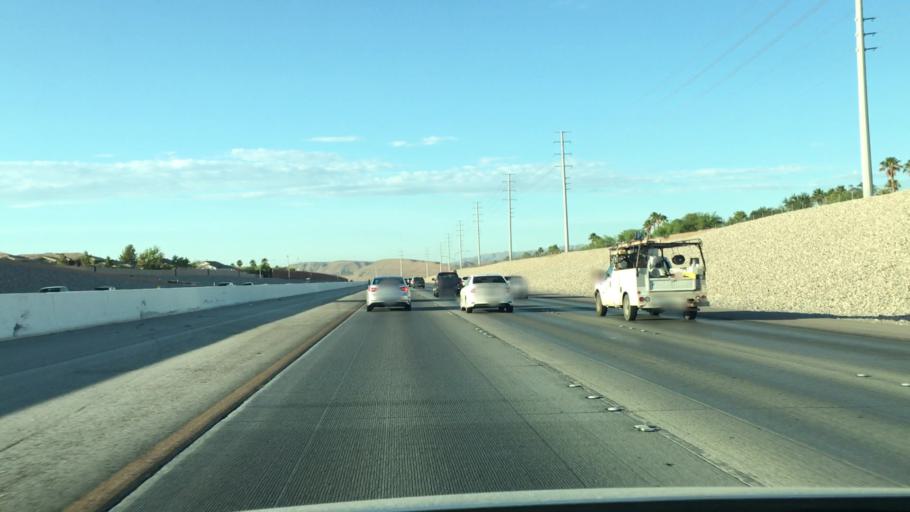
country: US
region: Nevada
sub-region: Clark County
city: Summerlin South
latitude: 36.1437
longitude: -115.3368
